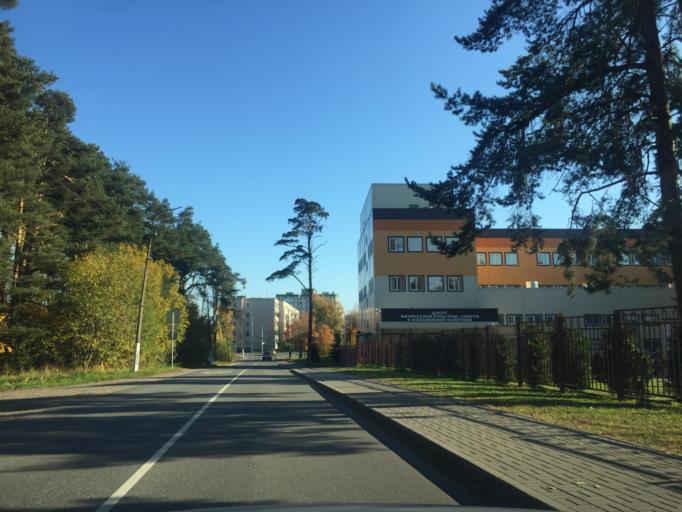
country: RU
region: Leningrad
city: Priozersk
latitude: 61.0387
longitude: 30.1148
